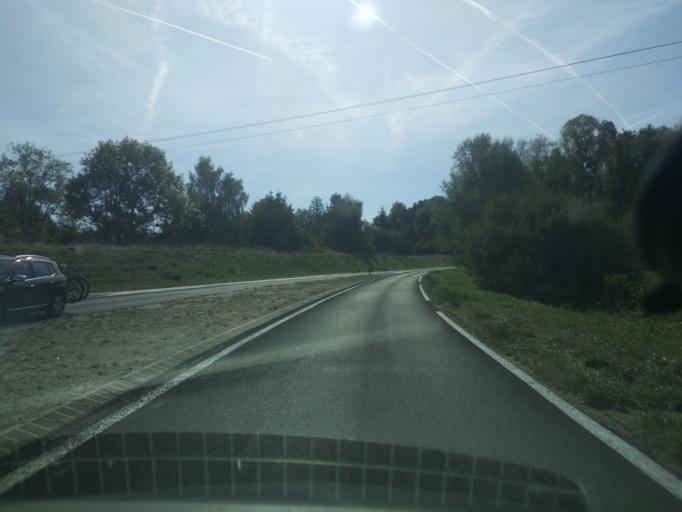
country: FR
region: Ile-de-France
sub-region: Departement de l'Essonne
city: Briis-sous-Forges
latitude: 48.6281
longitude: 2.1177
